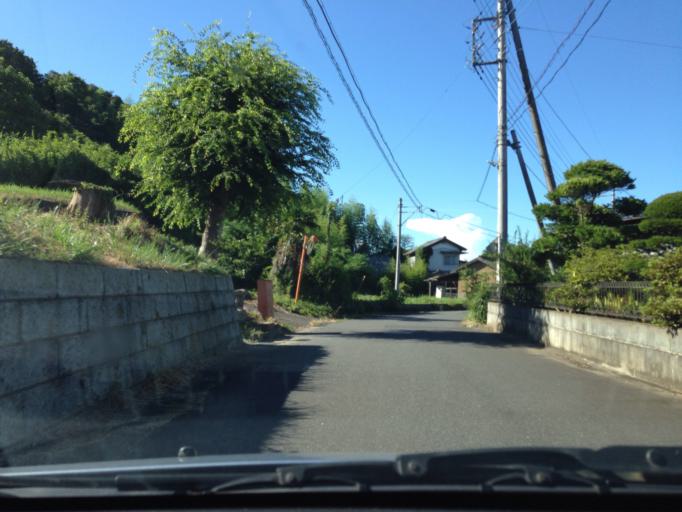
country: JP
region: Ibaraki
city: Inashiki
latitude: 36.0177
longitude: 140.3560
